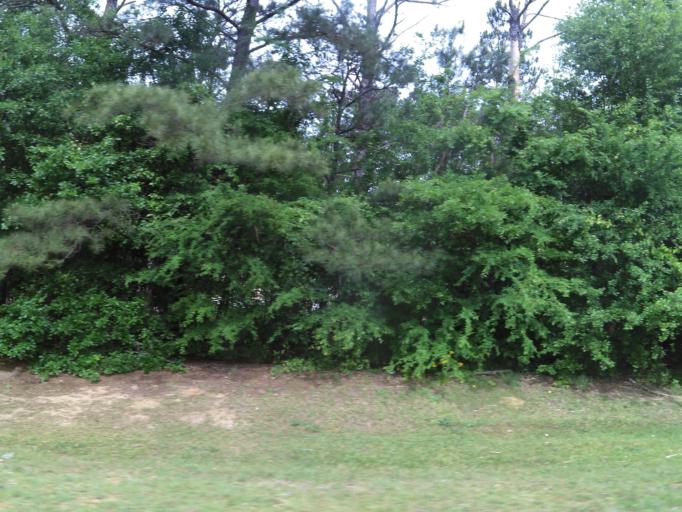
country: US
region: Georgia
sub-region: McDuffie County
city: Thomson
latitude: 33.3582
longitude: -82.4637
